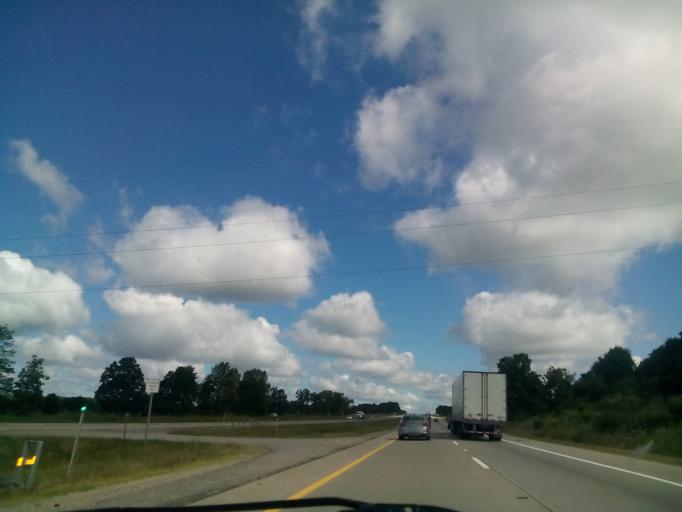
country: US
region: Michigan
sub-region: Genesee County
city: Linden
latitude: 42.7289
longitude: -83.7633
